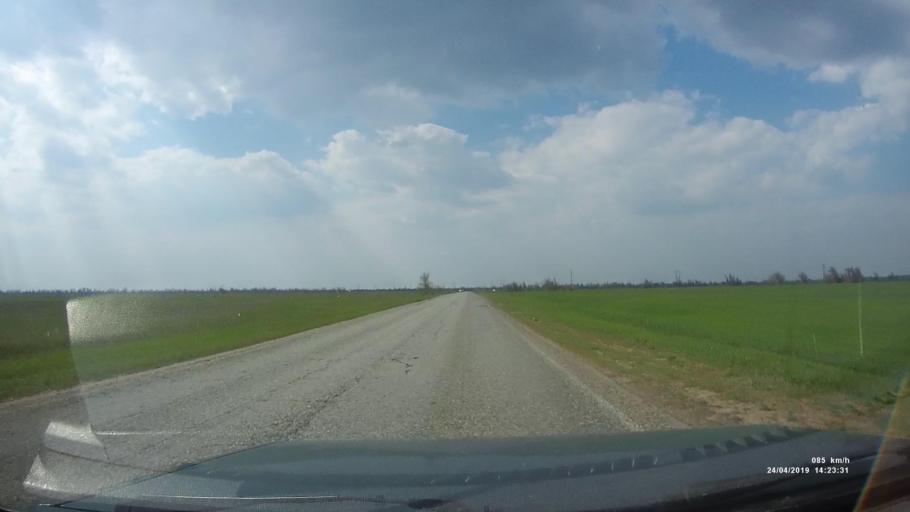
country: RU
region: Kalmykiya
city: Arshan'
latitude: 46.3230
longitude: 44.1128
